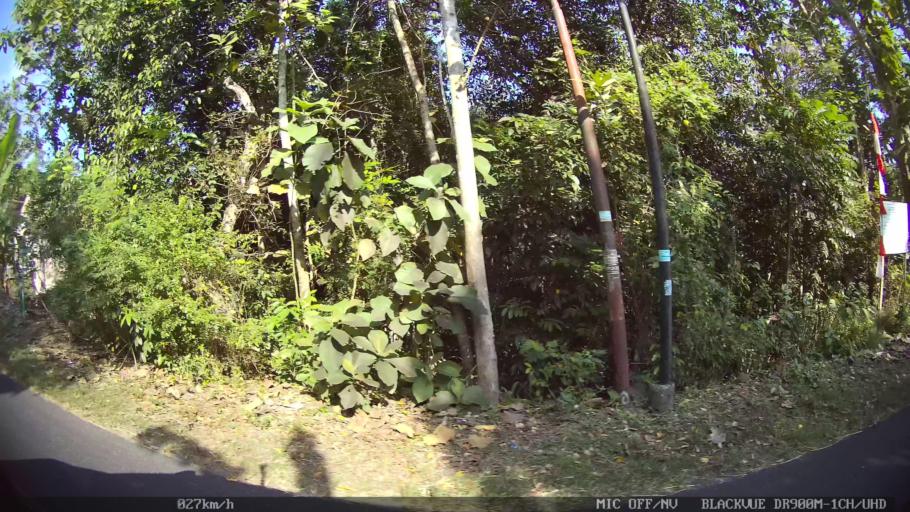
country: ID
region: Daerah Istimewa Yogyakarta
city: Kasihan
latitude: -7.8271
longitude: 110.2735
